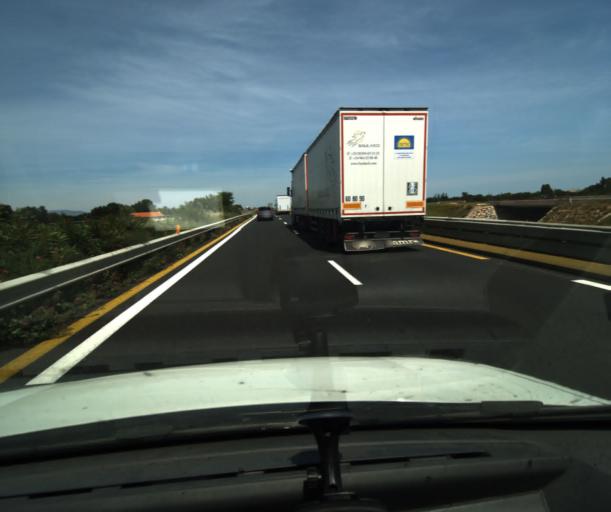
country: FR
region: Languedoc-Roussillon
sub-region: Departement des Pyrenees-Orientales
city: Saint-Esteve
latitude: 42.7093
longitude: 2.8685
